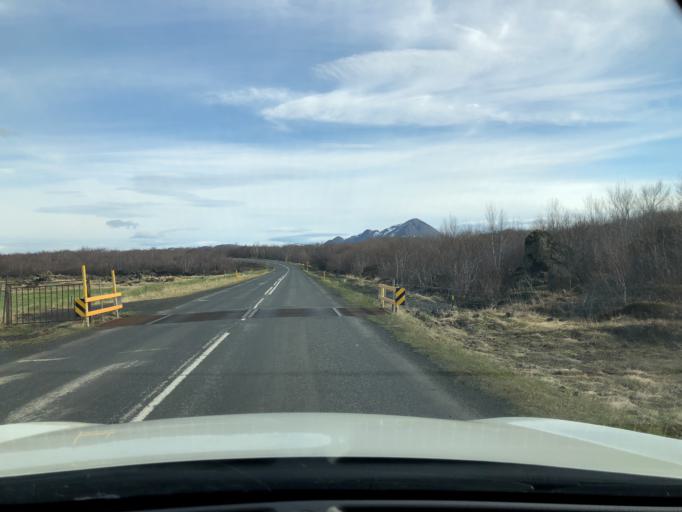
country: IS
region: Northeast
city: Laugar
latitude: 65.6265
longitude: -16.9184
